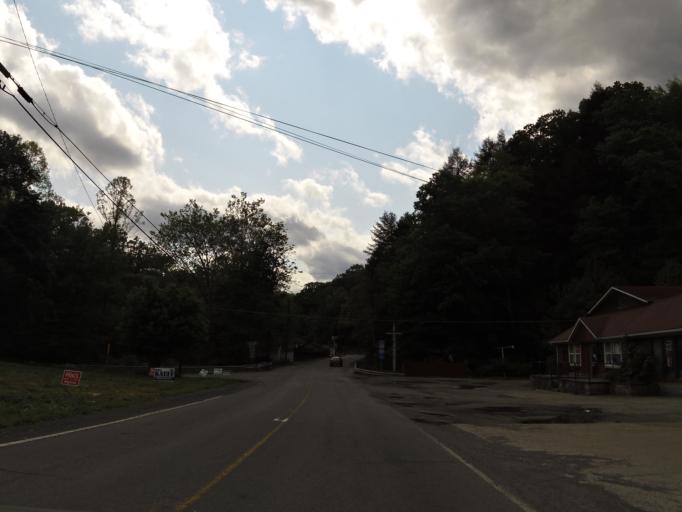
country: US
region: West Virginia
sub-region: Fayette County
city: Oak Hill
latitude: 37.9764
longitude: -81.2811
